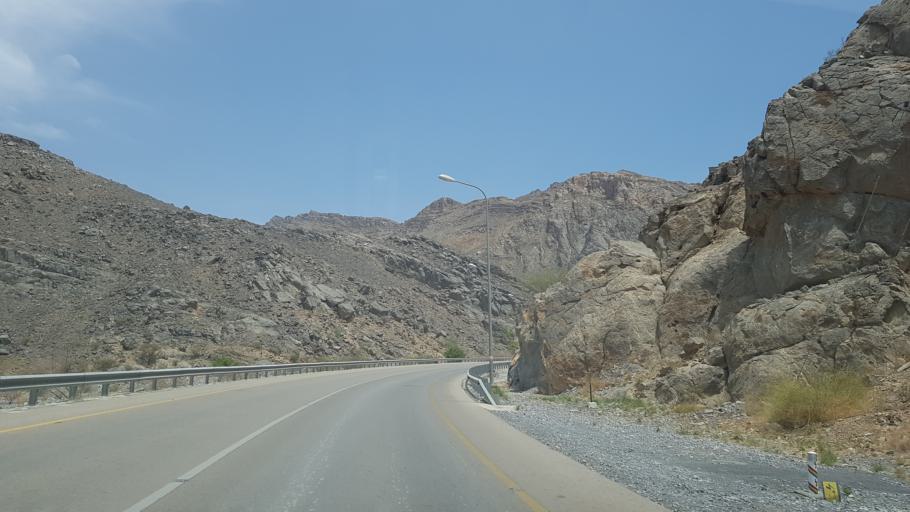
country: OM
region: Muhafazat ad Dakhiliyah
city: Izki
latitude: 22.9337
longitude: 57.6695
